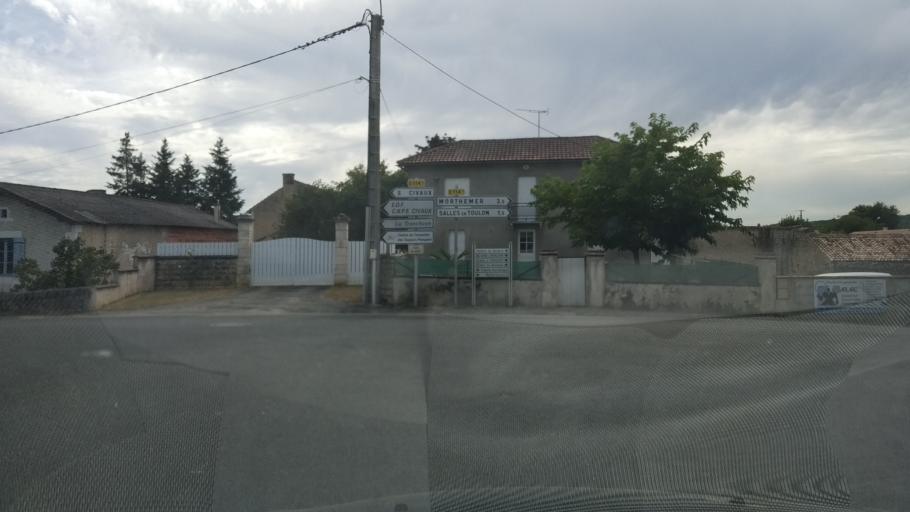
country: FR
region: Poitou-Charentes
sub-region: Departement de la Vienne
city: Chauvigny
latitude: 46.4816
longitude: 0.6475
